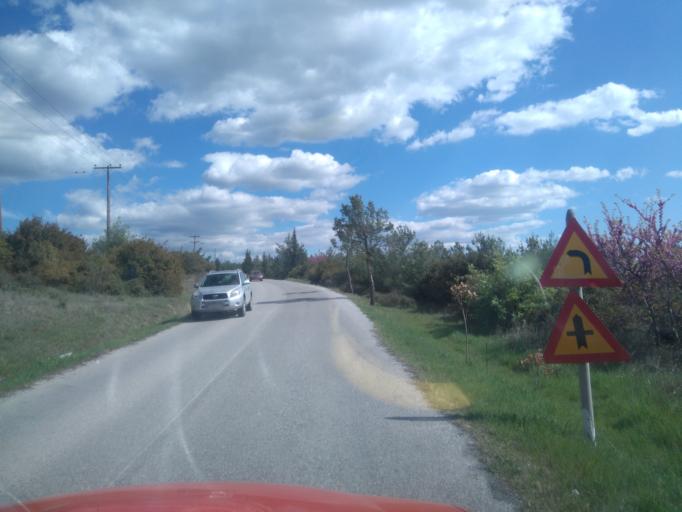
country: GR
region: Central Macedonia
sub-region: Nomos Thessalonikis
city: Pefka
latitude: 40.6443
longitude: 22.9956
